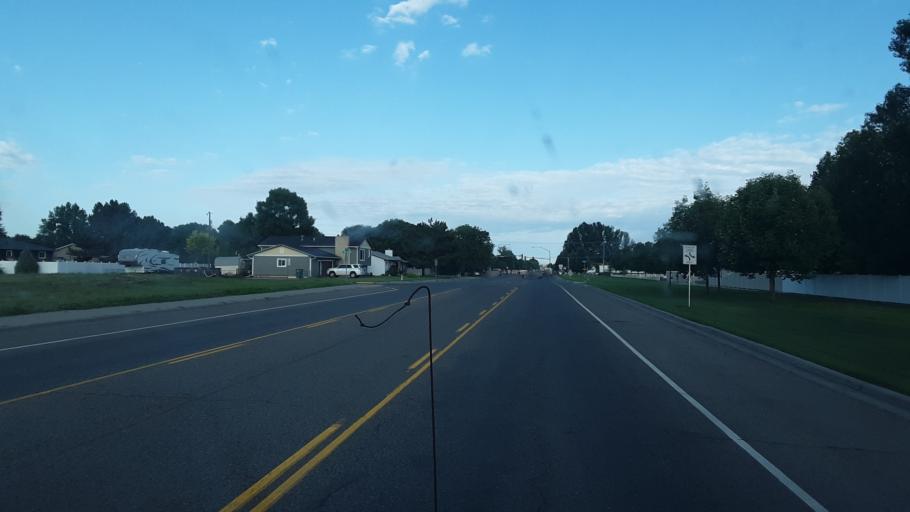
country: US
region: Montana
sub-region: Yellowstone County
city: Billings
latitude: 45.7624
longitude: -108.5932
